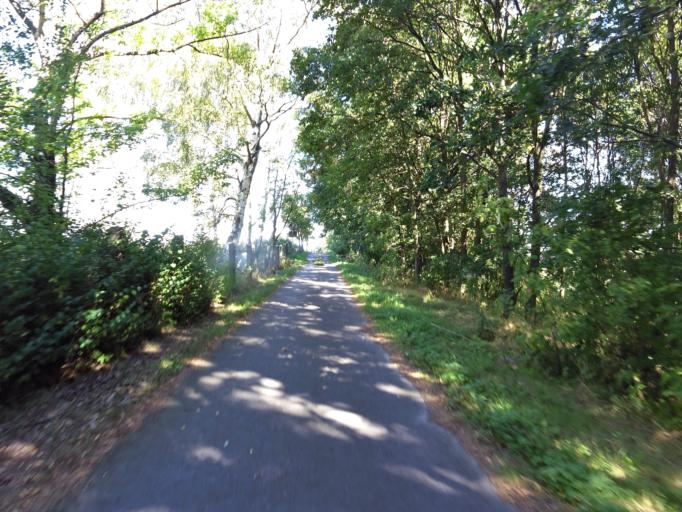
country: DE
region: Saxony-Anhalt
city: Pretzsch
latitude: 51.6931
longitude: 12.8270
